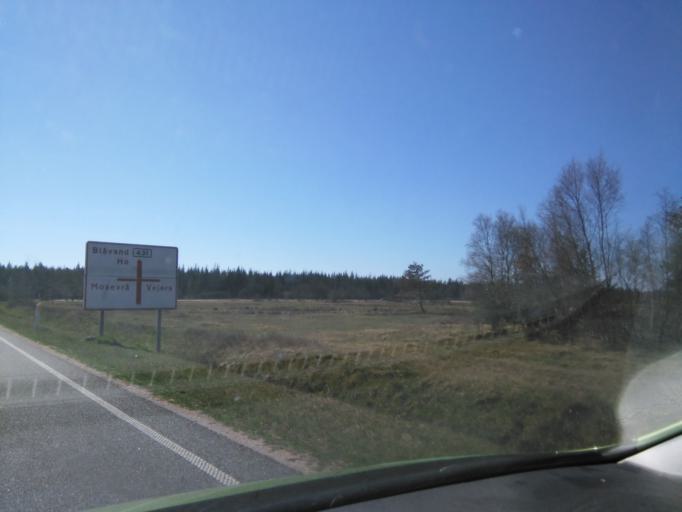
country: DK
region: South Denmark
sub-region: Varde Kommune
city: Oksbol
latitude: 55.6075
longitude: 8.2271
